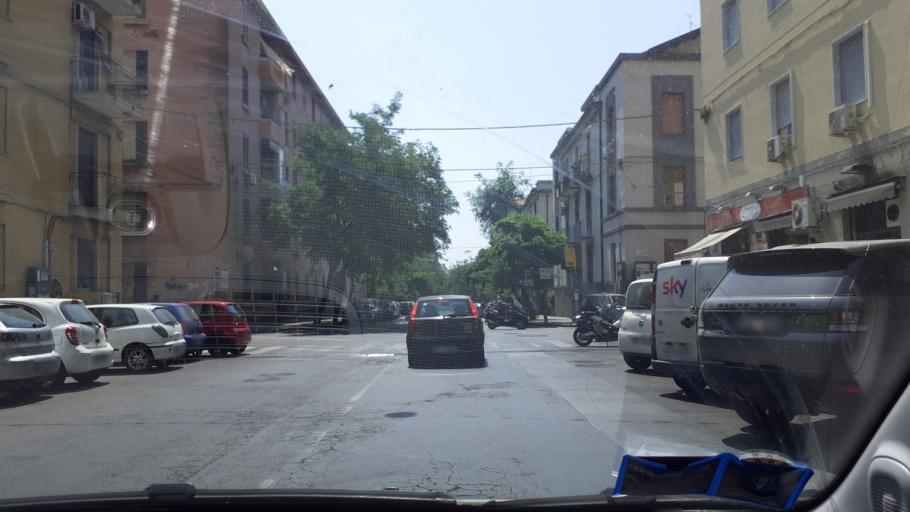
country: IT
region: Sicily
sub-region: Catania
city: Catania
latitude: 37.5131
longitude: 15.0744
